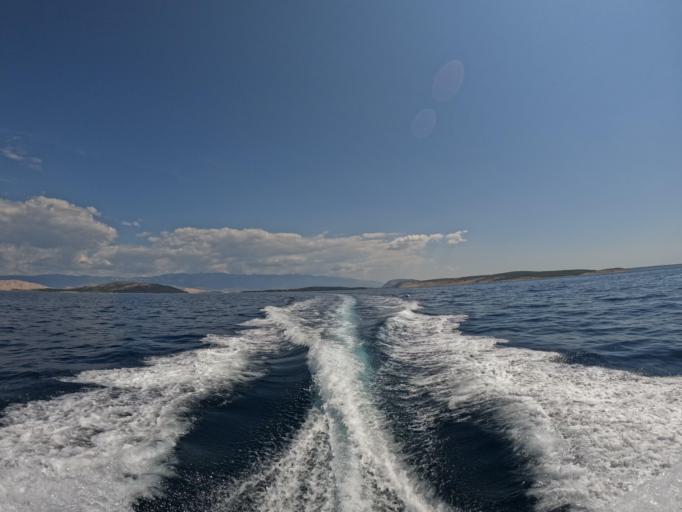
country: HR
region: Primorsko-Goranska
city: Lopar
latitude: 44.8676
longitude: 14.6801
